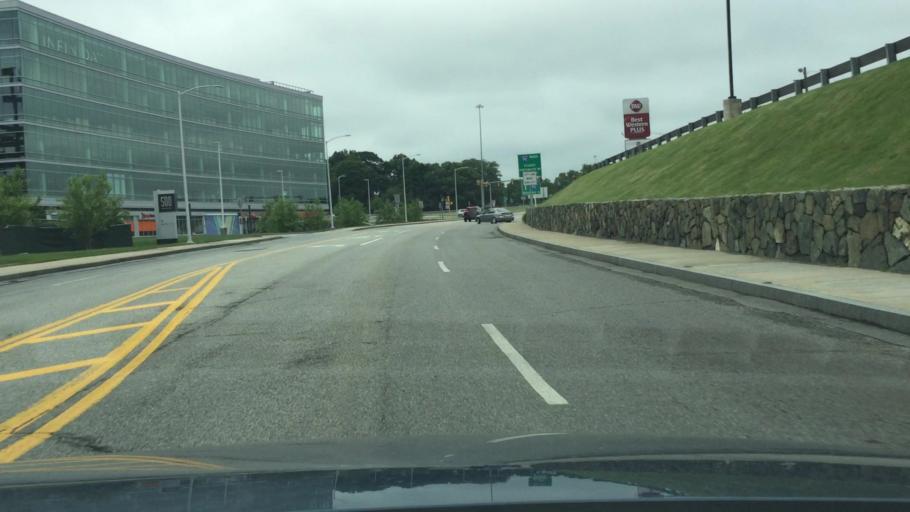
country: US
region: Massachusetts
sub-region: Middlesex County
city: Waltham
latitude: 42.3970
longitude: -71.2573
